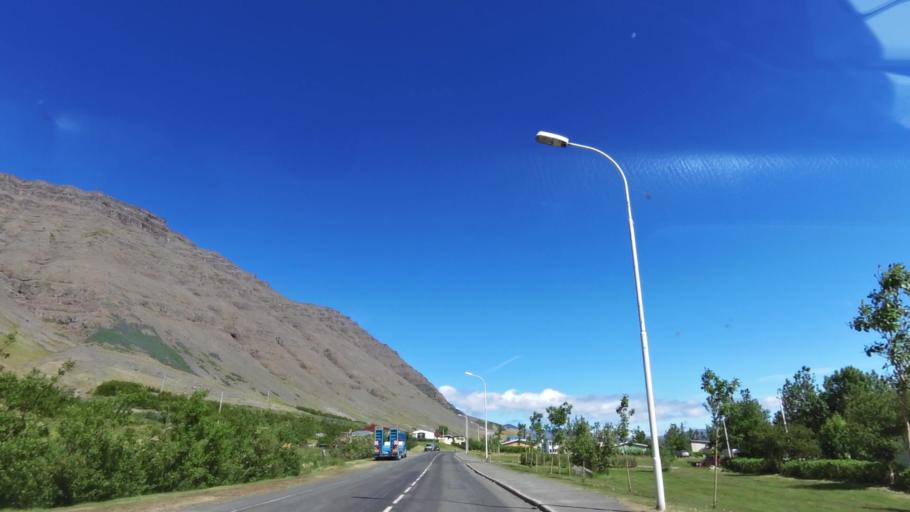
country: IS
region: Westfjords
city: Isafjoerdur
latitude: 65.6784
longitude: -23.6119
